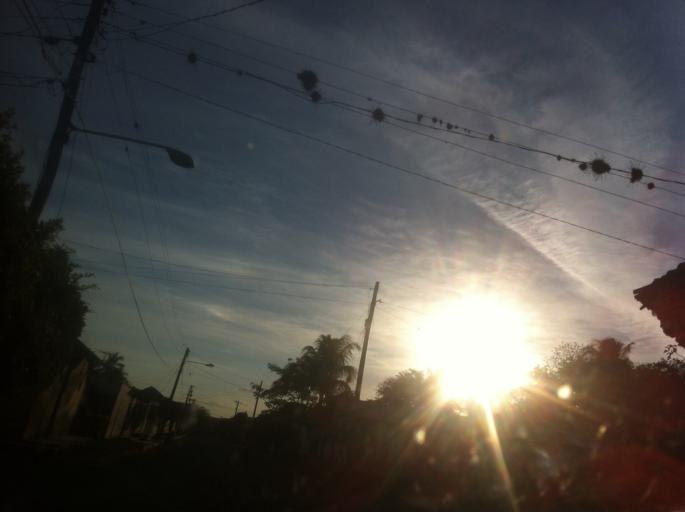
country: NI
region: Rivas
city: Potosi
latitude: 11.4947
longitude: -85.8573
